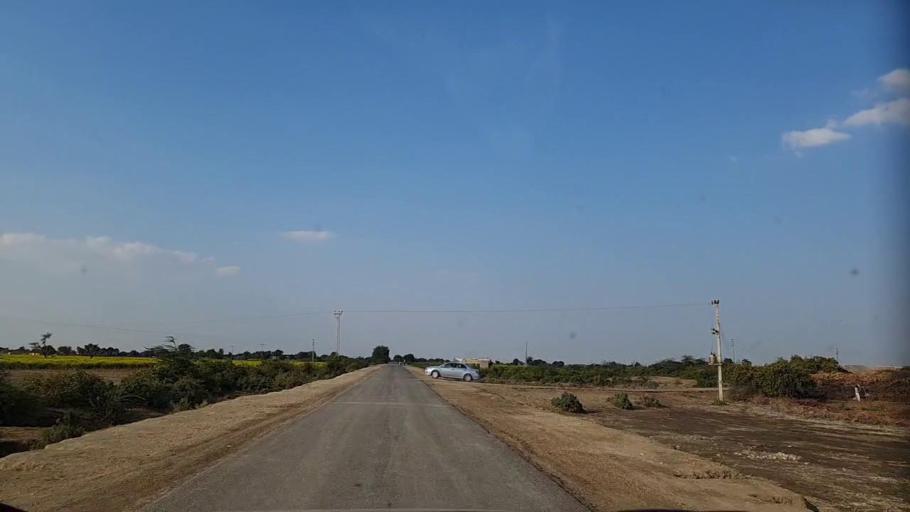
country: PK
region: Sindh
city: Pithoro
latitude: 25.6800
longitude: 69.2266
